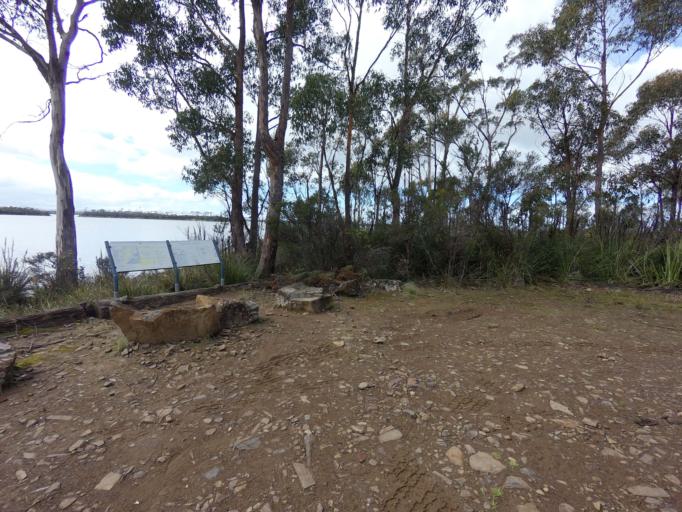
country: AU
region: Tasmania
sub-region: Huon Valley
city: Geeveston
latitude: -43.4819
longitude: 146.9391
